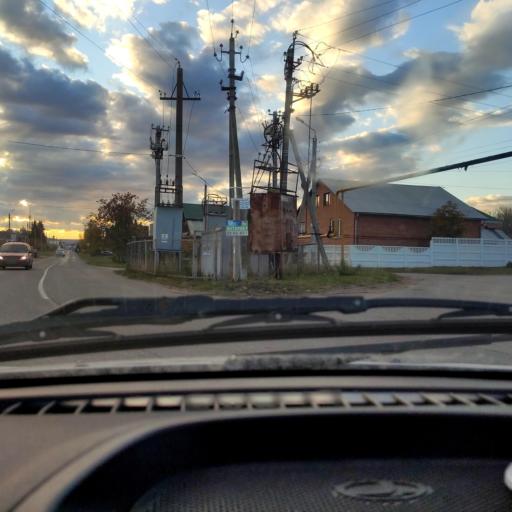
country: RU
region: Samara
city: Zhigulevsk
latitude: 53.4663
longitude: 49.6370
